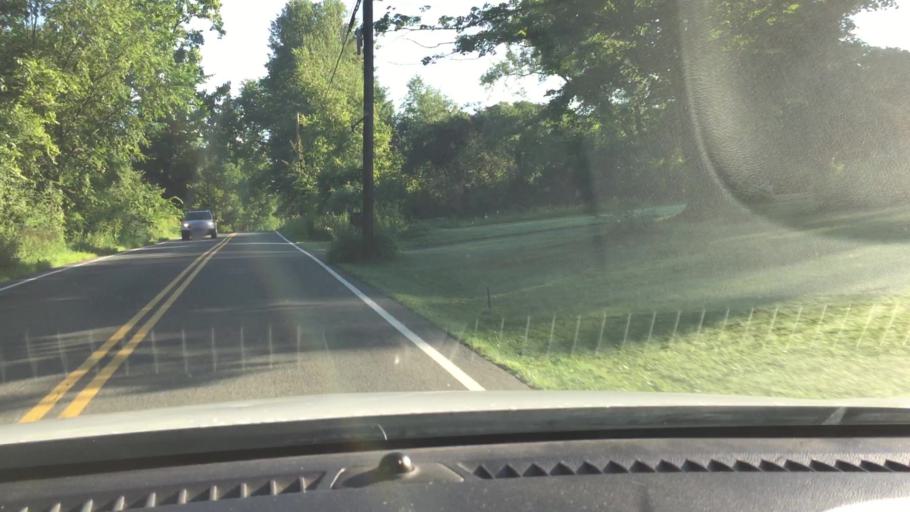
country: US
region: Massachusetts
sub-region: Berkshire County
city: Pittsfield
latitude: 42.3973
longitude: -73.2341
